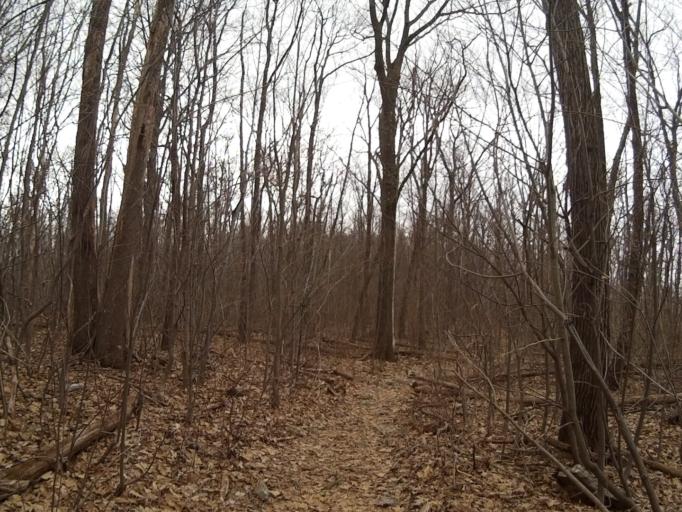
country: US
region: Pennsylvania
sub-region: Centre County
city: Lemont
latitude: 40.8172
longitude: -77.7905
